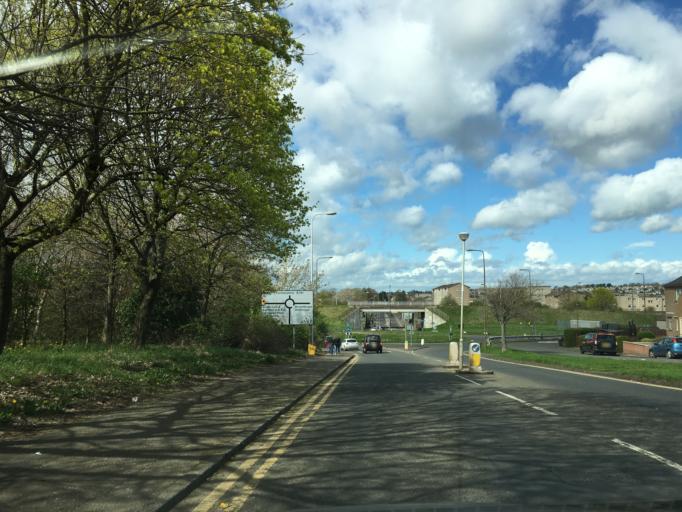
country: GB
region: Scotland
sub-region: Edinburgh
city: Colinton
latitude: 55.9285
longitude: -3.2846
